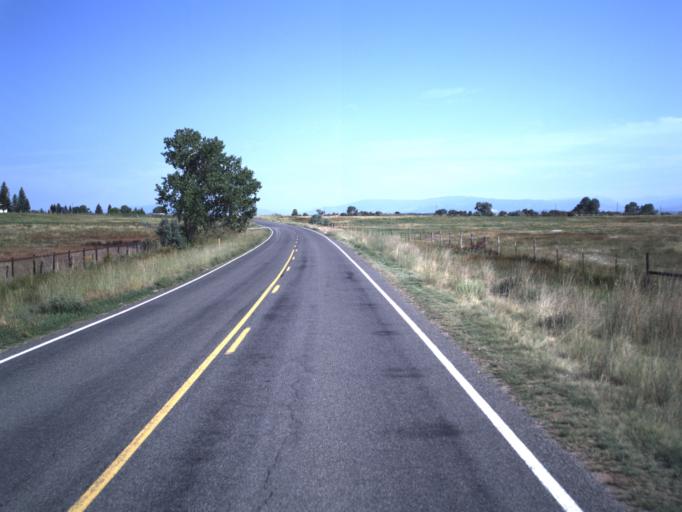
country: US
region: Utah
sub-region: Duchesne County
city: Duchesne
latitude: 40.3057
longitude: -110.2417
